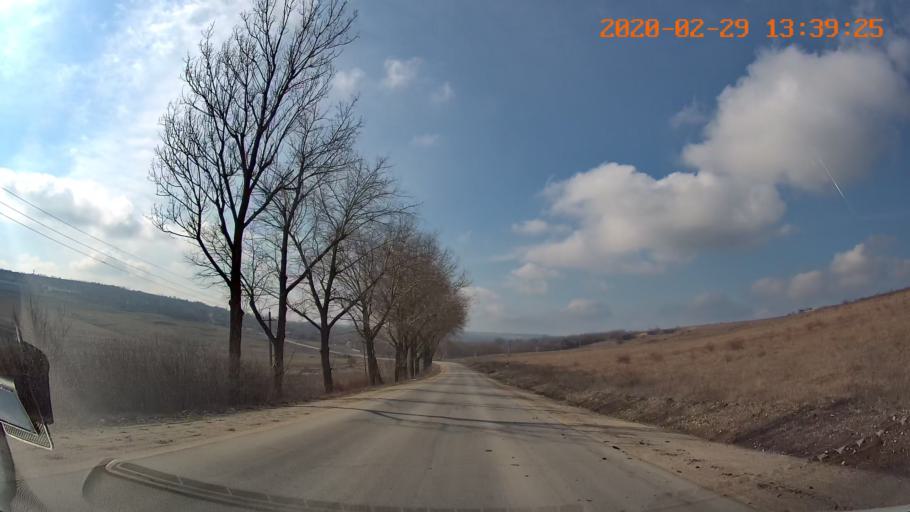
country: MD
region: Floresti
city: Leninskiy
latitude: 47.8515
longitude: 28.5818
